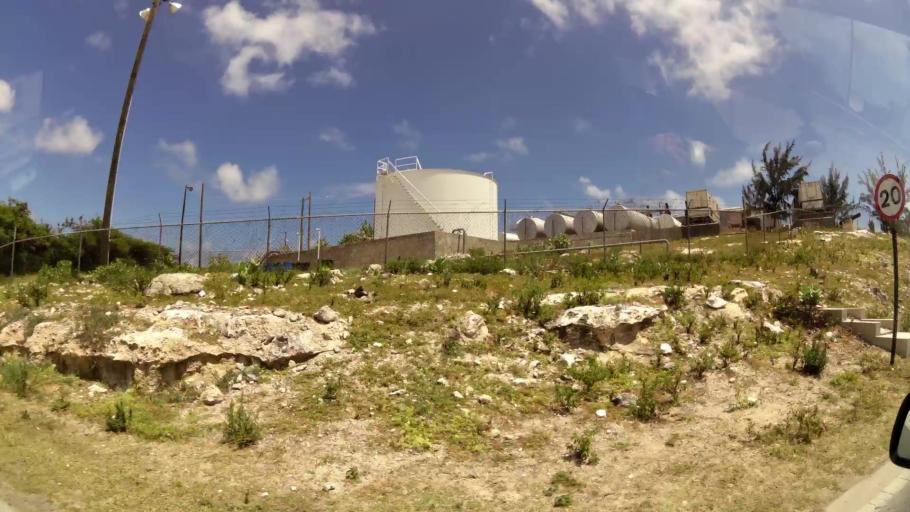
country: TC
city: Cockburn Town
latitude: 21.4337
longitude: -71.1460
